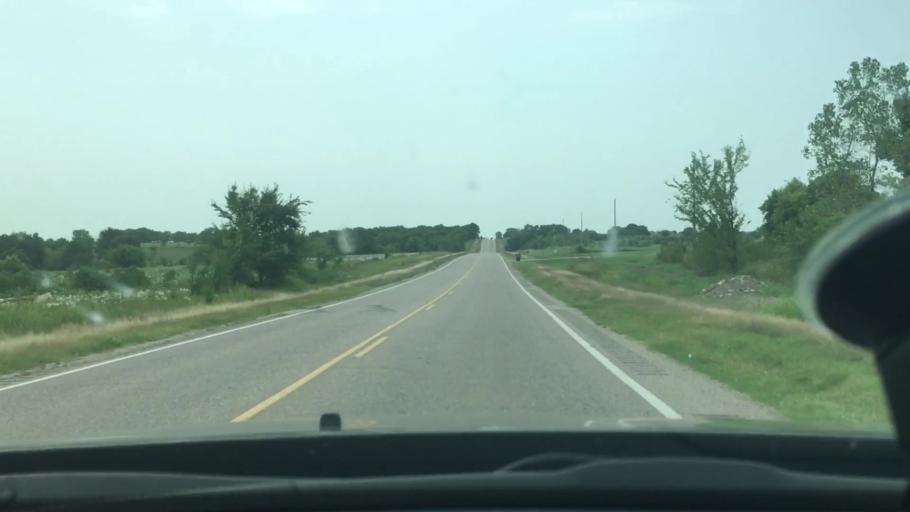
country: US
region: Oklahoma
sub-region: Marshall County
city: Madill
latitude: 34.0598
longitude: -96.7611
